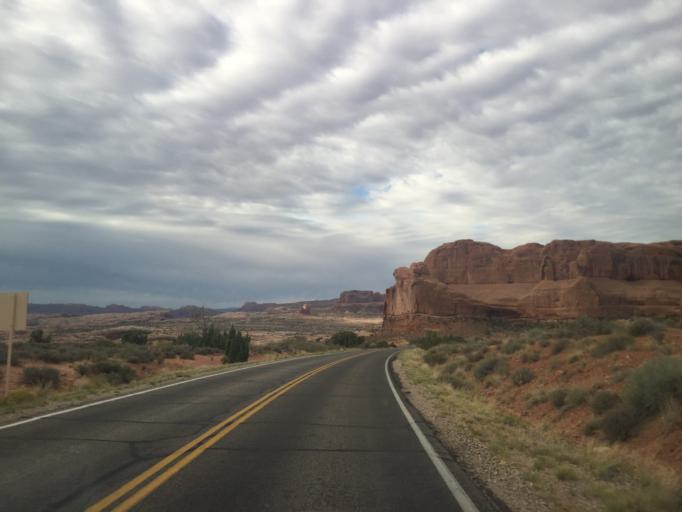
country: US
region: Utah
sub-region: Grand County
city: Moab
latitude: 38.6646
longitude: -109.5876
